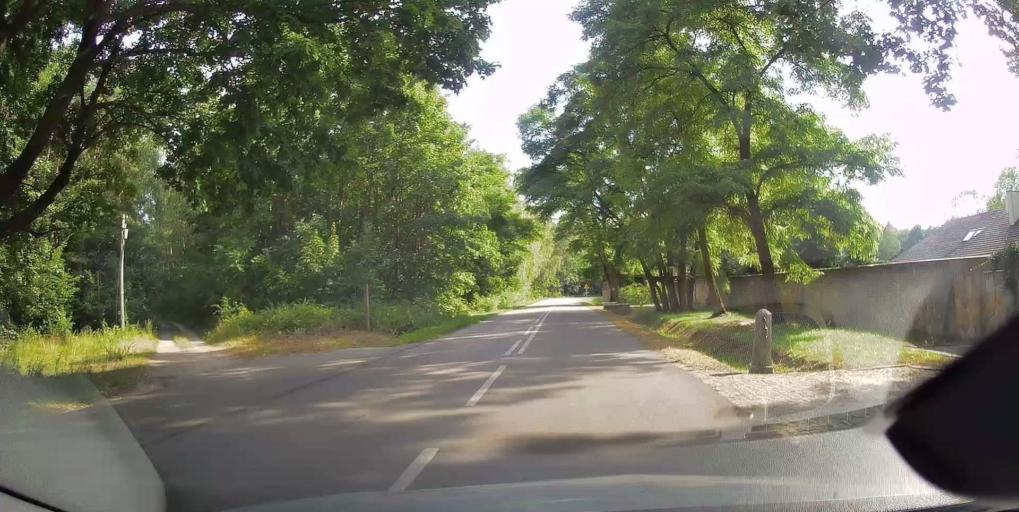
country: PL
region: Lodz Voivodeship
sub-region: Powiat opoczynski
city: Mniszkow
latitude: 51.4099
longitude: 20.0481
